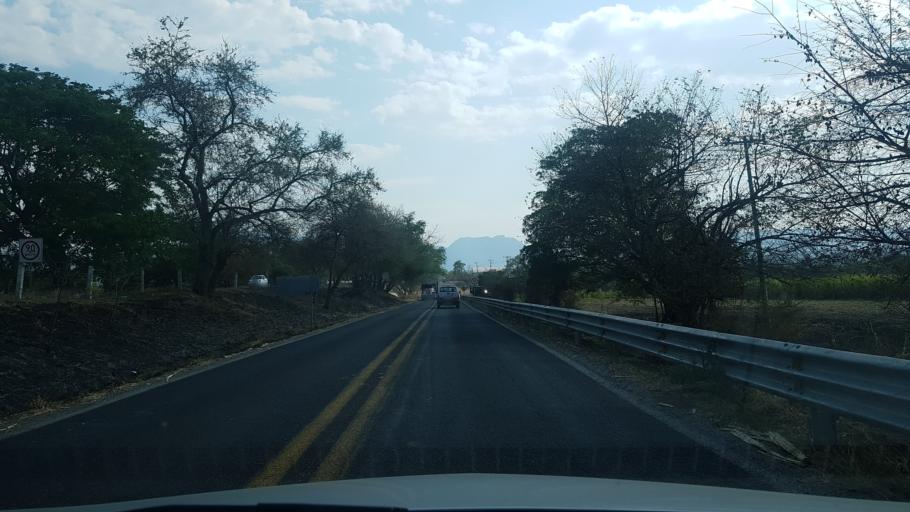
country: MX
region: Morelos
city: Puente de Ixtla
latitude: 18.6283
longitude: -99.3280
